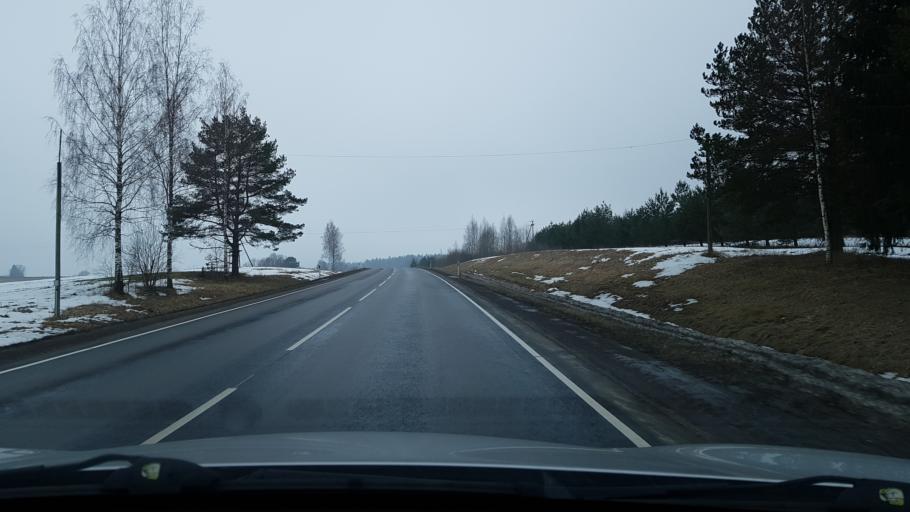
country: EE
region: Valgamaa
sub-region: Valga linn
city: Valga
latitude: 57.8464
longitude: 26.1291
